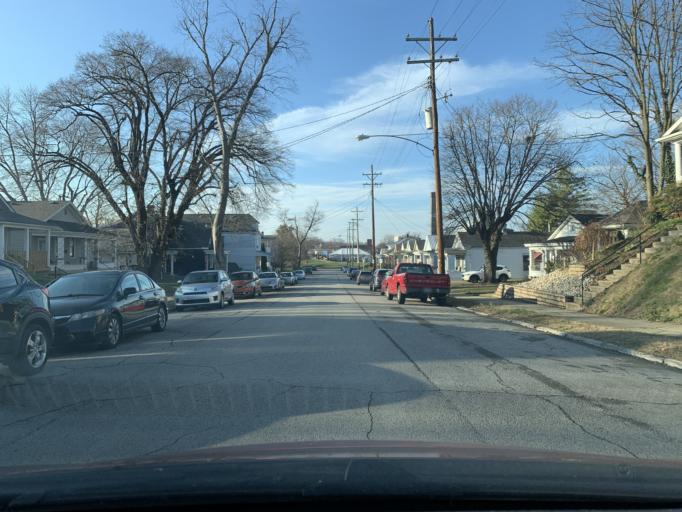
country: US
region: Kentucky
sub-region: Jefferson County
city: Audubon Park
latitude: 38.2272
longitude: -85.7377
